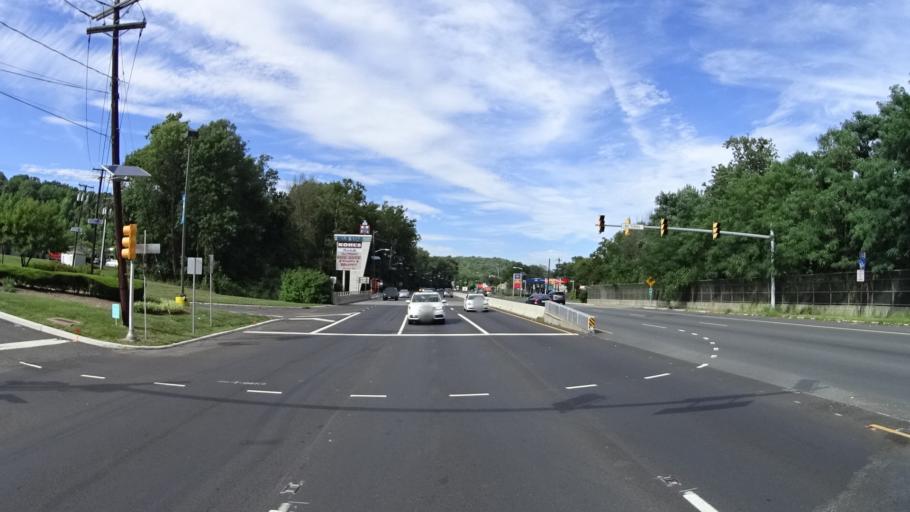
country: US
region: New Jersey
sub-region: Union County
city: Plainfield
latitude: 40.6489
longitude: -74.4070
